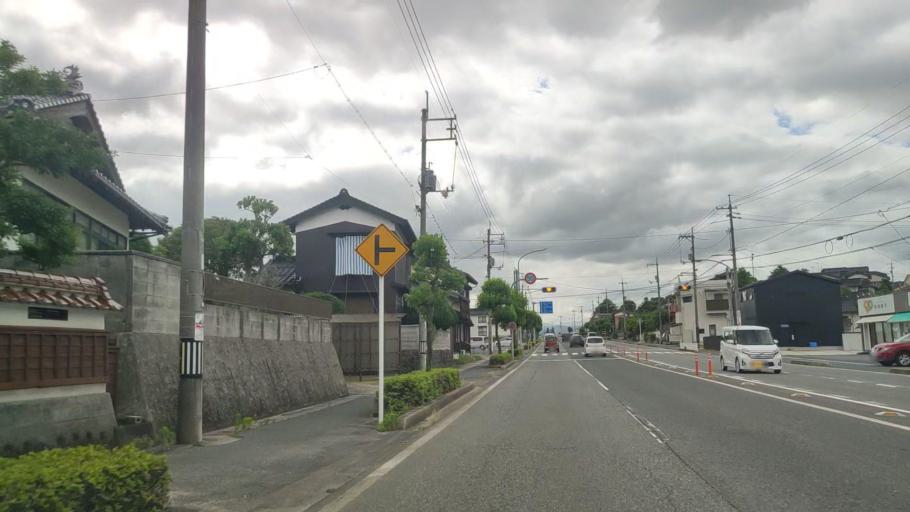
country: JP
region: Tottori
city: Yonago
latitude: 35.4039
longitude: 133.3689
